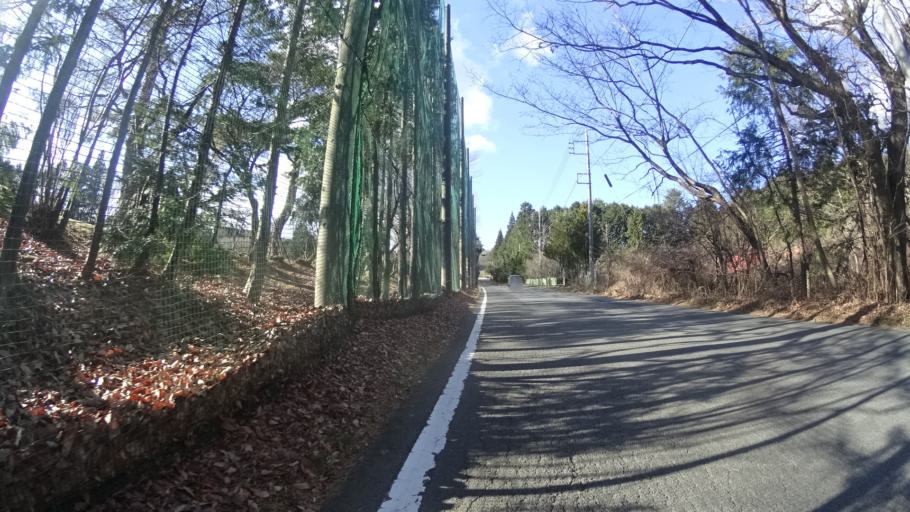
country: JP
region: Shizuoka
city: Gotemba
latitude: 35.3469
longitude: 138.8820
